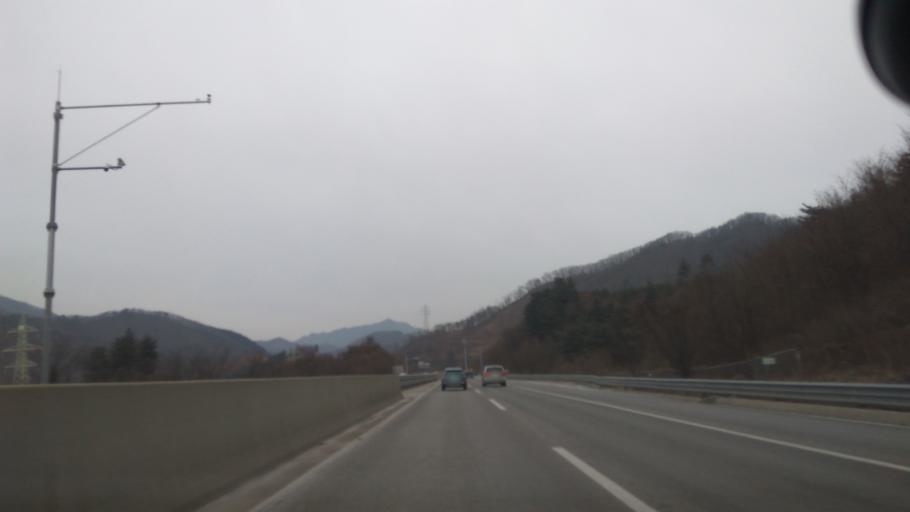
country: KR
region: Gyeonggi-do
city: Hwado
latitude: 37.6338
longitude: 127.3934
